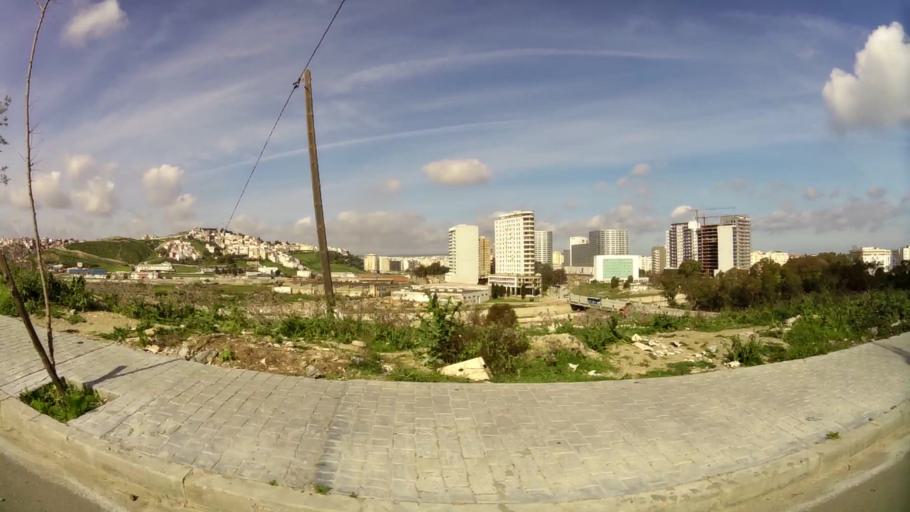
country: MA
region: Tanger-Tetouan
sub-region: Tanger-Assilah
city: Tangier
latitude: 35.7700
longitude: -5.7779
